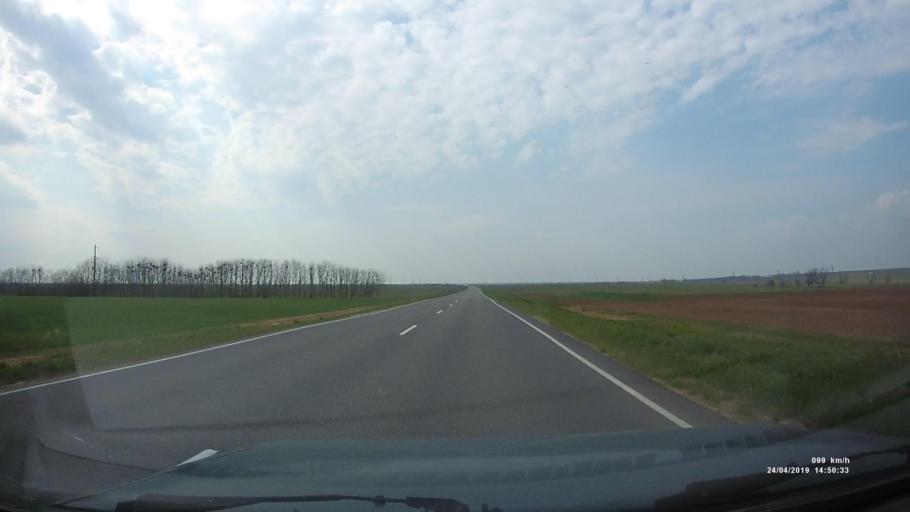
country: RU
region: Rostov
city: Remontnoye
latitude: 46.5181
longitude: 43.7174
